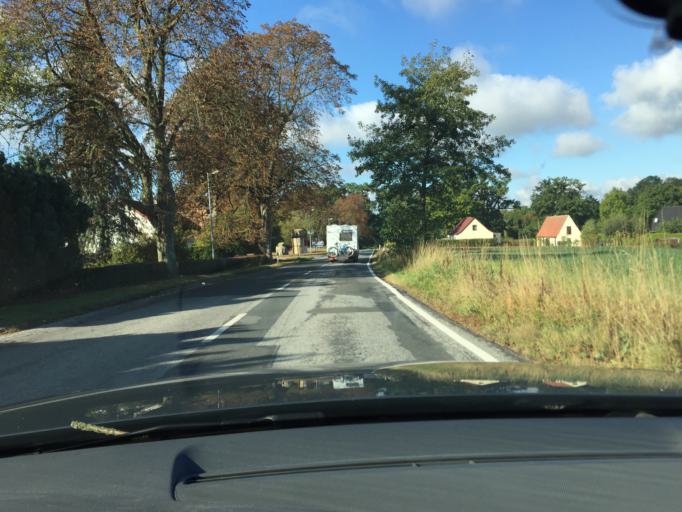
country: DE
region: Mecklenburg-Vorpommern
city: Lalendorf
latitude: 53.6824
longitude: 12.3659
